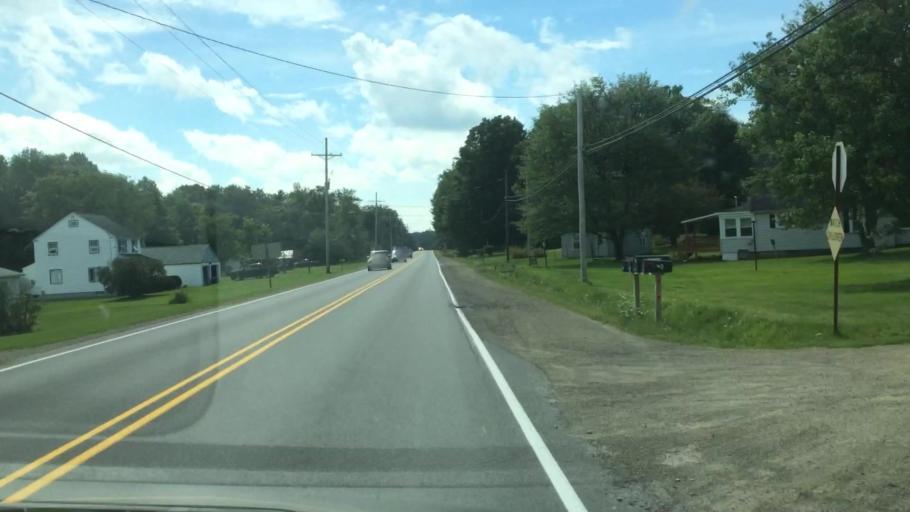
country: US
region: Pennsylvania
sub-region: McKean County
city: Bradford
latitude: 41.8776
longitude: -78.5787
